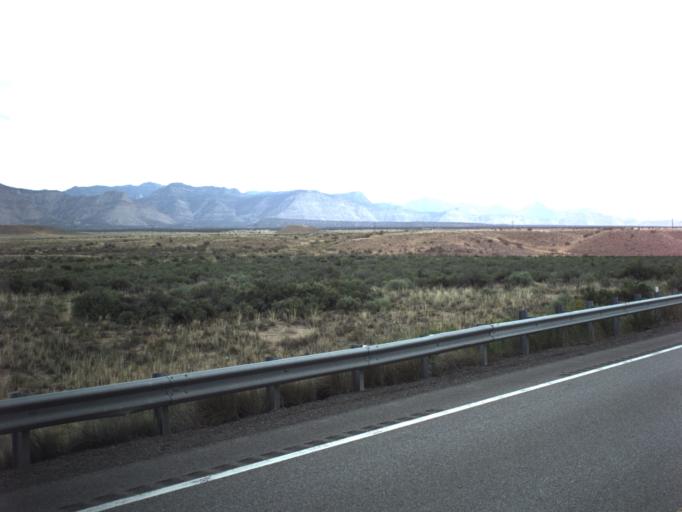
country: US
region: Utah
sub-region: Carbon County
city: East Carbon City
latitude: 39.4546
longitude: -110.4800
